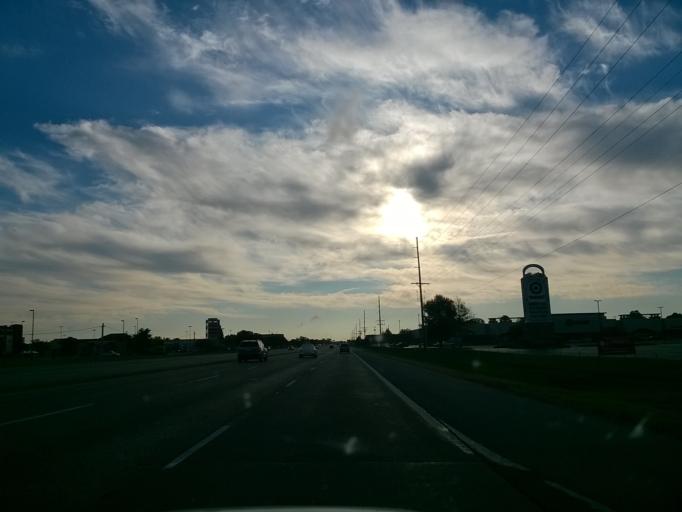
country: US
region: Indiana
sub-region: Vanderburgh County
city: Melody Hill
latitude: 37.9765
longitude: -87.4723
